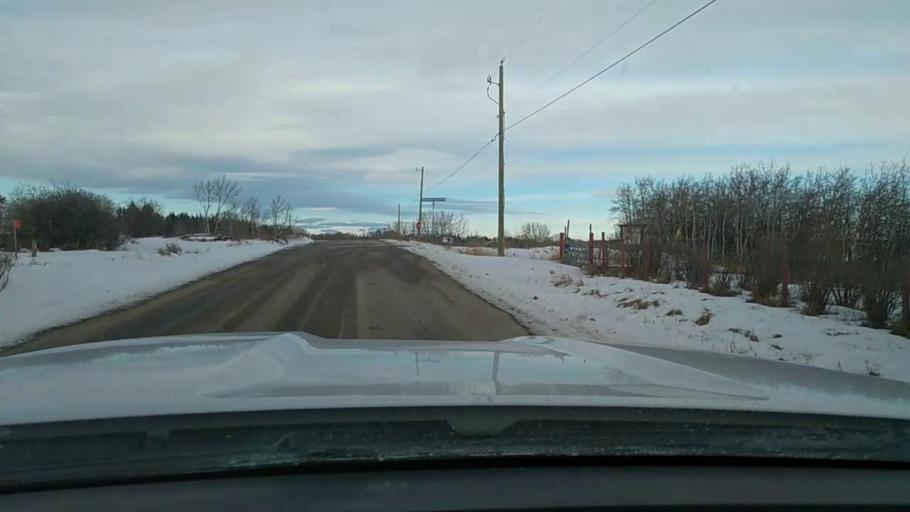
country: CA
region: Alberta
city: Cochrane
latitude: 51.1498
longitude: -114.2674
